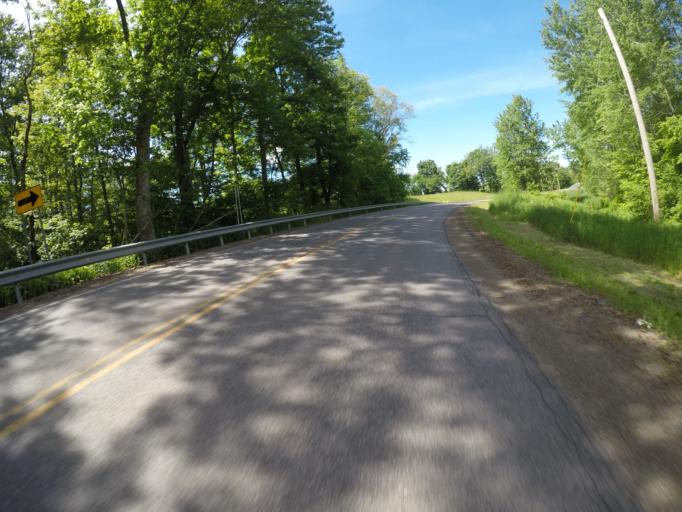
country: US
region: New York
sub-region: Delaware County
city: Delhi
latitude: 42.1616
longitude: -74.7981
